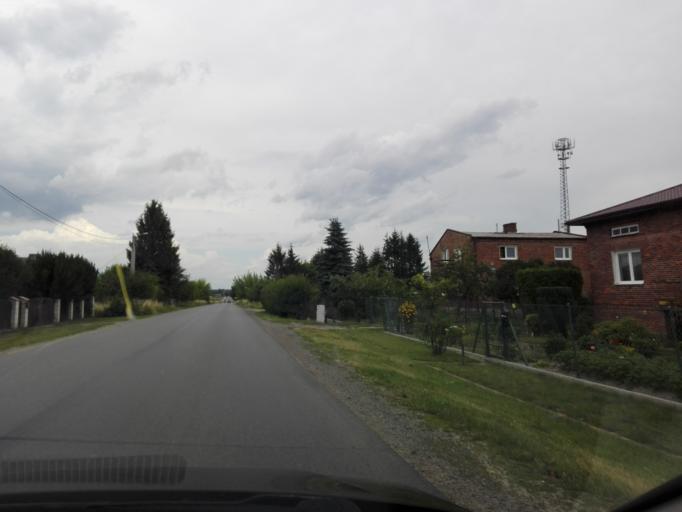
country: PL
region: Lublin Voivodeship
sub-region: Powiat pulawski
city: Kurow
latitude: 51.3976
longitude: 22.1987
